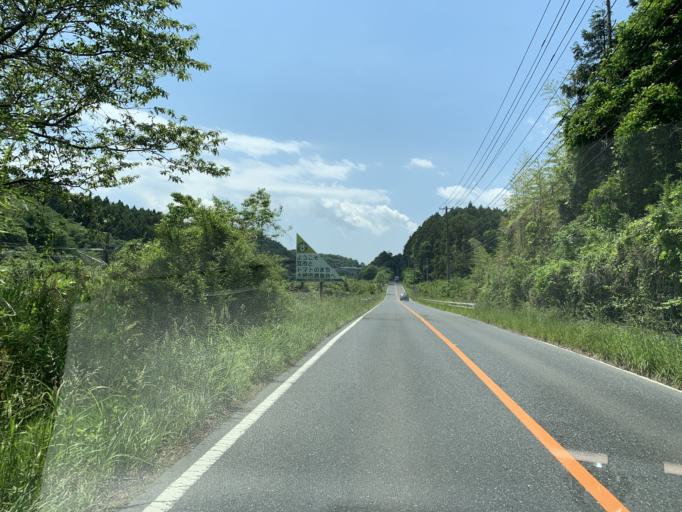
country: JP
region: Miyagi
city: Kogota
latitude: 38.4947
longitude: 141.0877
